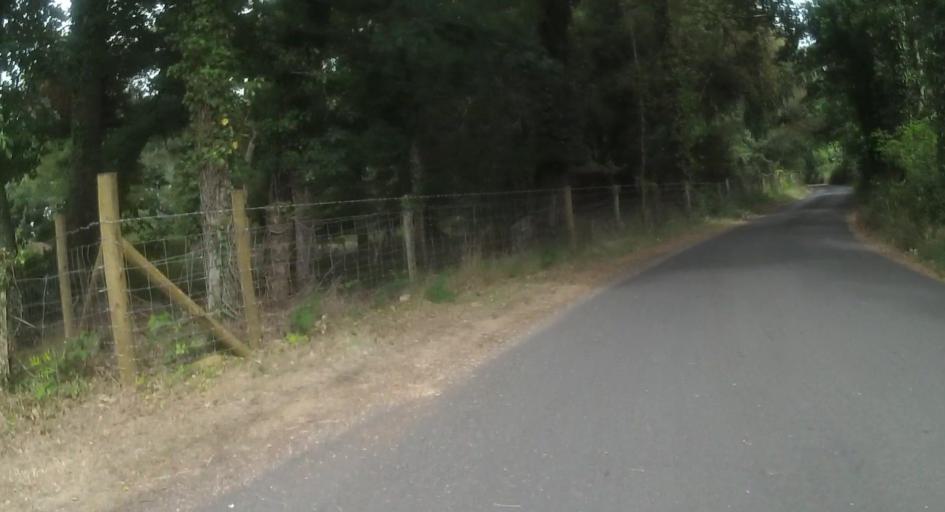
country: GB
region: England
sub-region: Dorset
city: Wool
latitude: 50.7171
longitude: -2.1931
